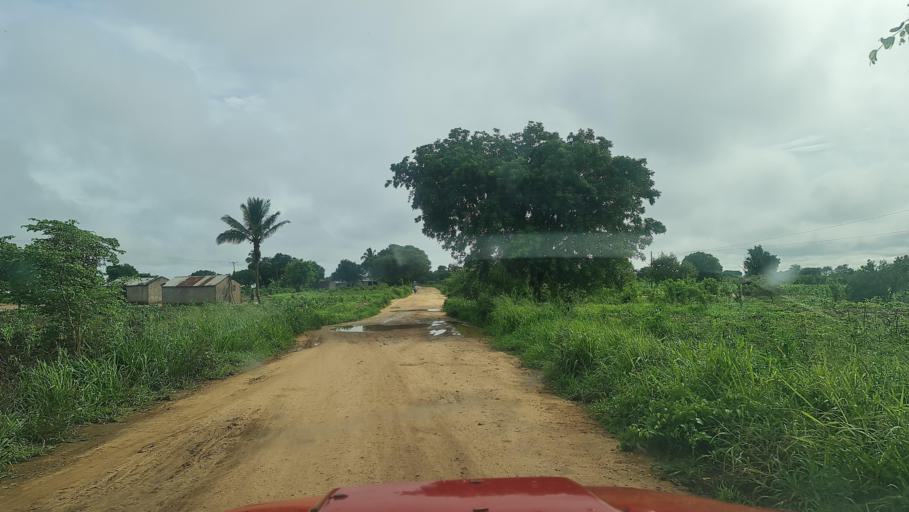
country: MW
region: Southern Region
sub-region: Nsanje District
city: Nsanje
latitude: -17.2918
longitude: 35.6001
